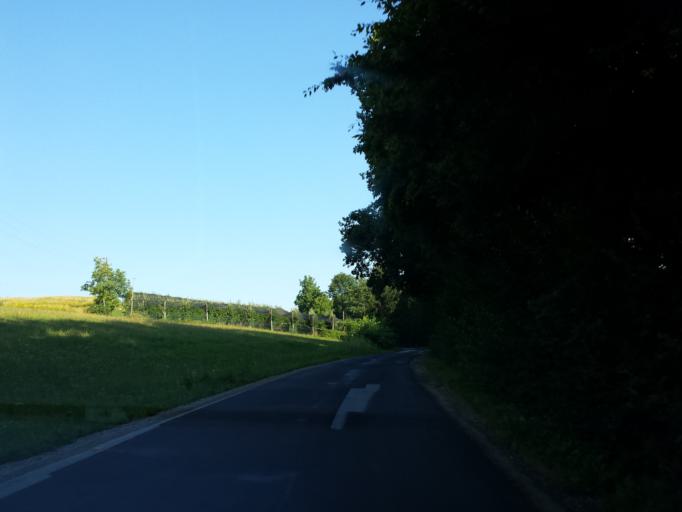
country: AT
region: Styria
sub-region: Politischer Bezirk Weiz
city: Gleisdorf
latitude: 47.1196
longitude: 15.6813
